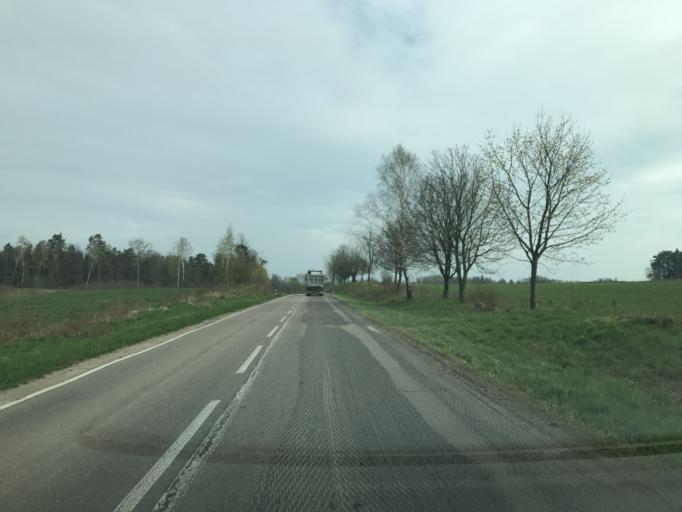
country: PL
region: Warmian-Masurian Voivodeship
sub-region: Powiat ostrodzki
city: Gierzwald
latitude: 53.5557
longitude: 20.0925
